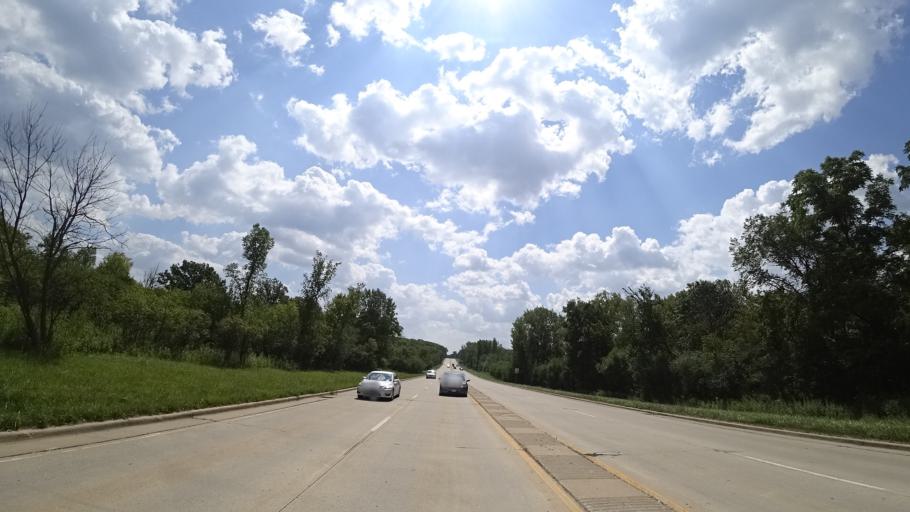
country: US
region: Illinois
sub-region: Cook County
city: Crestwood
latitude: 41.6395
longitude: -87.7767
